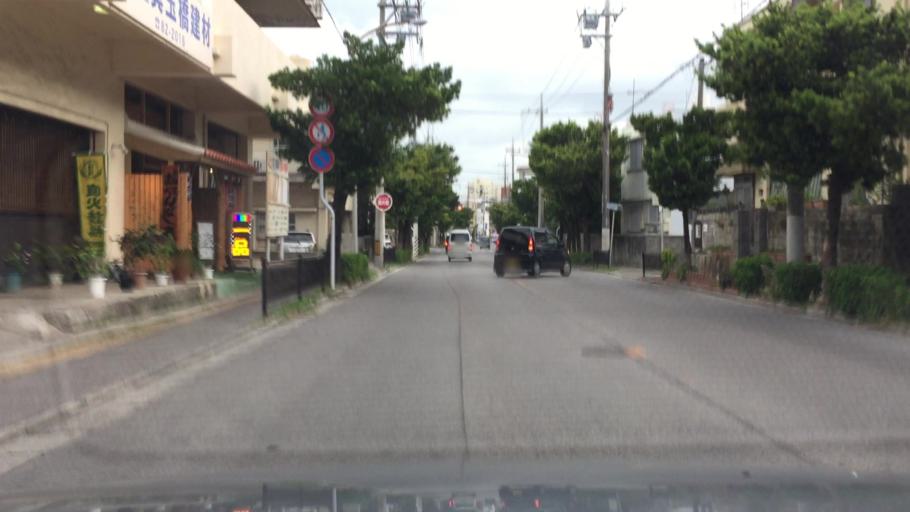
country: JP
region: Okinawa
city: Ishigaki
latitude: 24.3446
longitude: 124.1560
